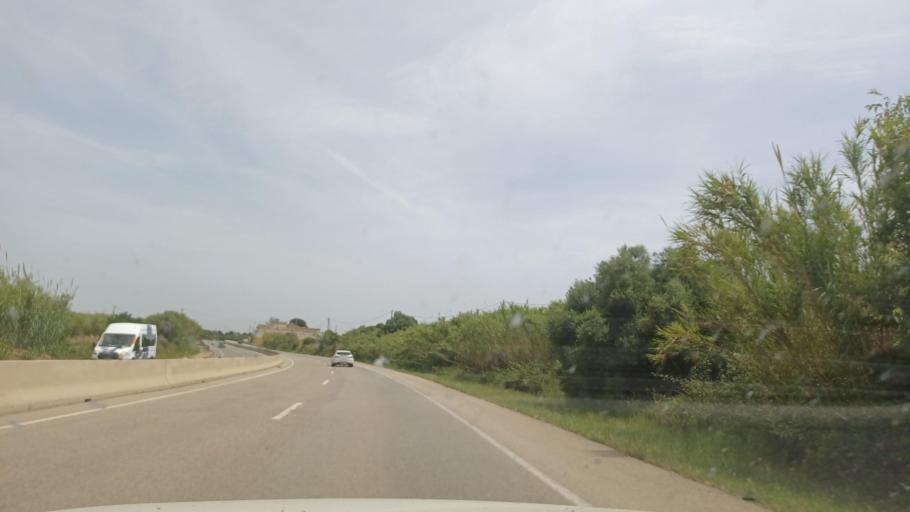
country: ES
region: Catalonia
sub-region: Provincia de Tarragona
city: Vila-seca
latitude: 41.1305
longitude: 1.1467
